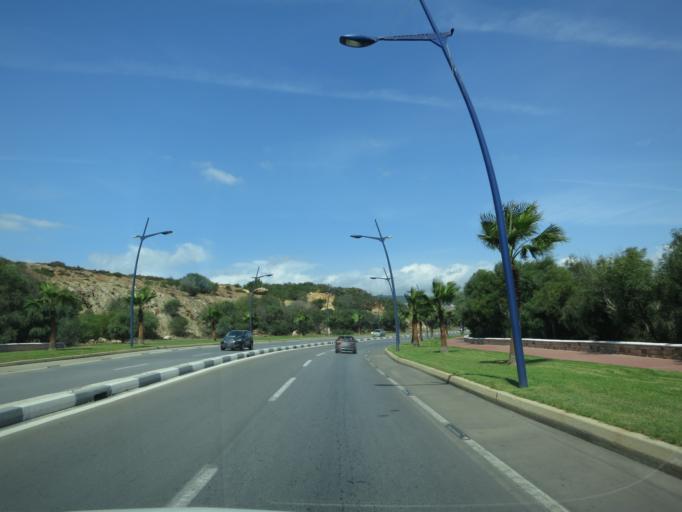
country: ES
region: Ceuta
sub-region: Ceuta
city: Ceuta
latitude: 35.7827
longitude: -5.3502
